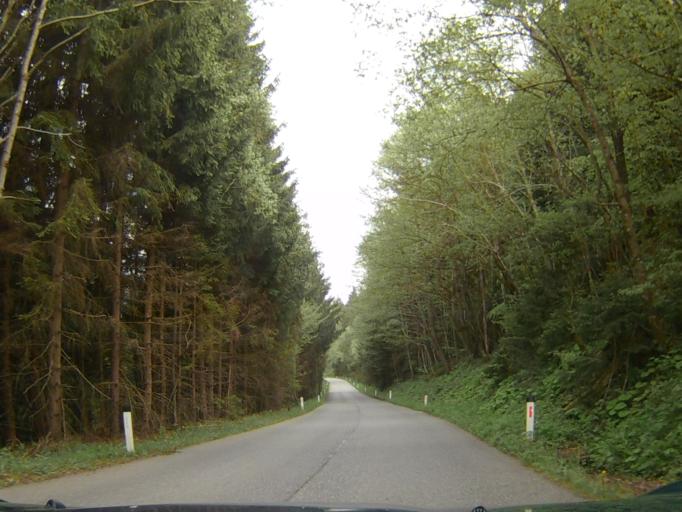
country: AT
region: Carinthia
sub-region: Politischer Bezirk Villach Land
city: Stockenboi
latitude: 46.7360
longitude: 13.5714
